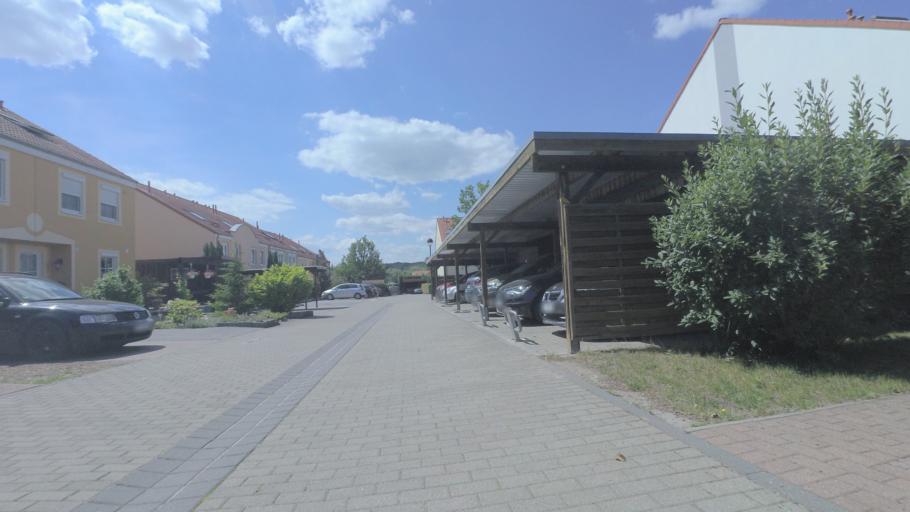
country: DE
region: Brandenburg
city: Rangsdorf
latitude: 52.2983
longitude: 13.4358
